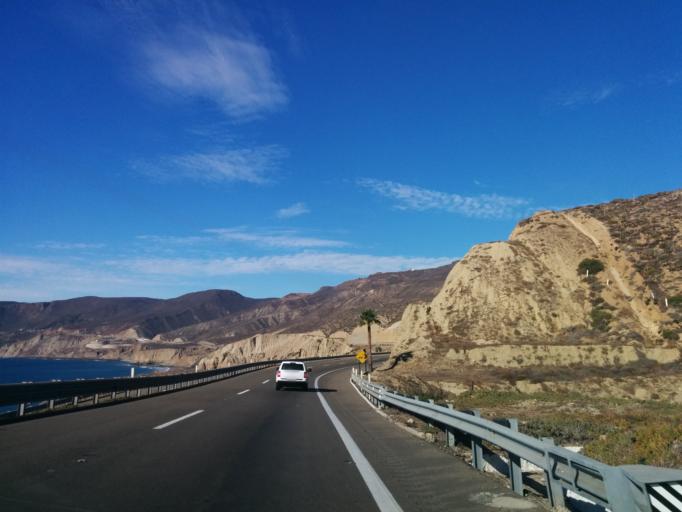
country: MX
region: Baja California
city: El Sauzal
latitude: 31.9525
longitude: -116.7574
